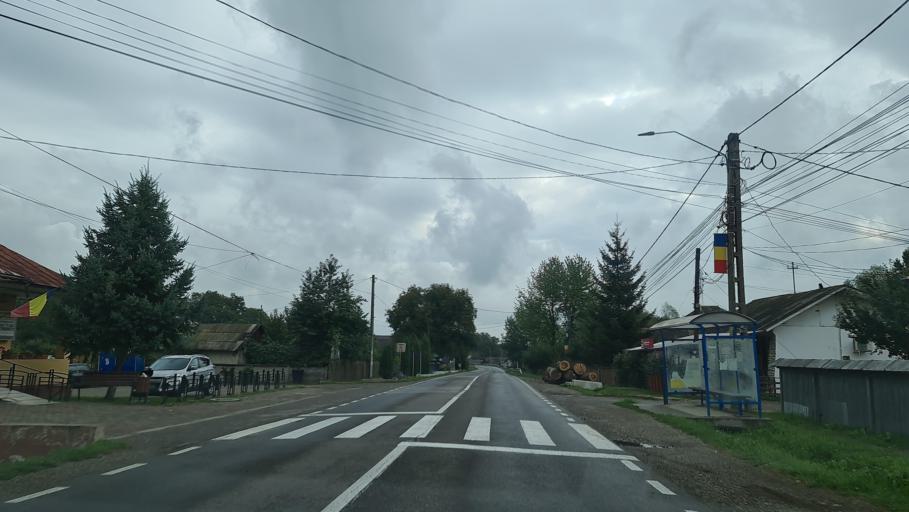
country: RO
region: Neamt
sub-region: Comuna Borlesti
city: Mastacan
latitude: 46.7796
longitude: 26.5126
